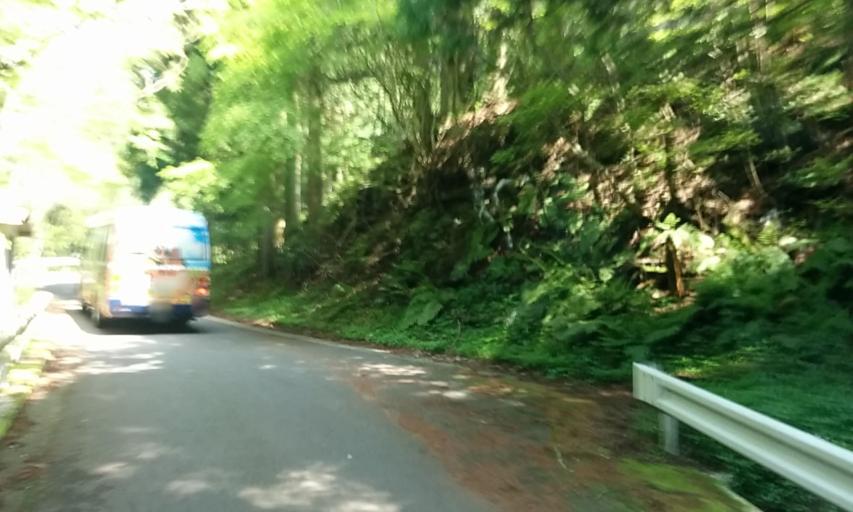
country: JP
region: Ehime
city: Niihama
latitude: 33.8679
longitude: 133.2956
